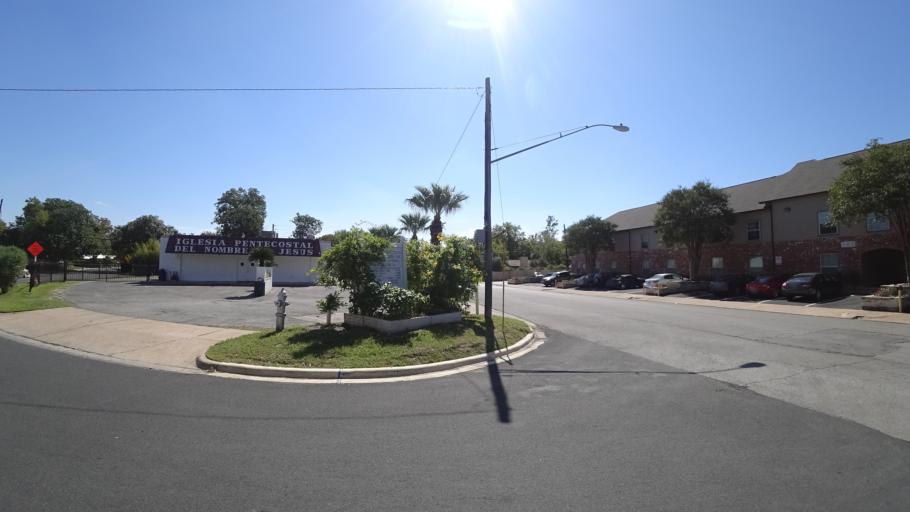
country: US
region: Texas
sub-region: Travis County
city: Austin
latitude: 30.3105
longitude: -97.7058
